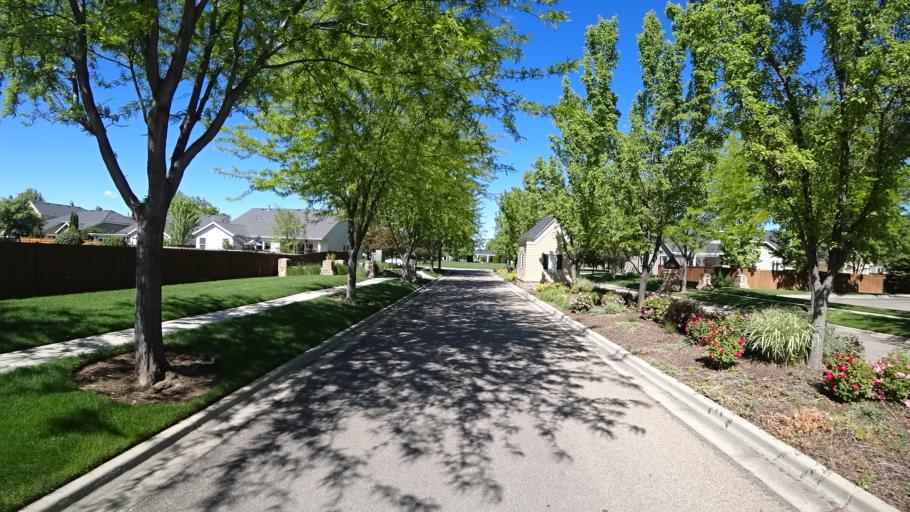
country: US
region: Idaho
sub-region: Ada County
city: Meridian
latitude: 43.6394
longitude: -116.3756
